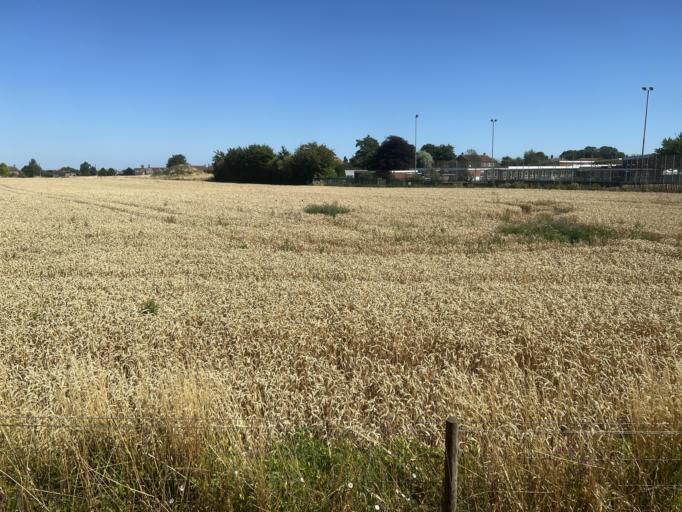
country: GB
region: England
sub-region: Lincolnshire
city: Wainfleet All Saints
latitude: 53.1072
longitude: 0.2304
